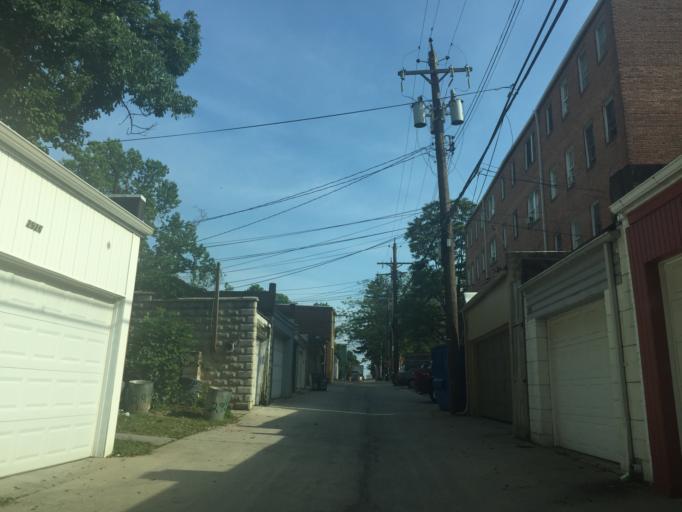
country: US
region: Maryland
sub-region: City of Baltimore
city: Baltimore
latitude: 39.3240
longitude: -76.6166
